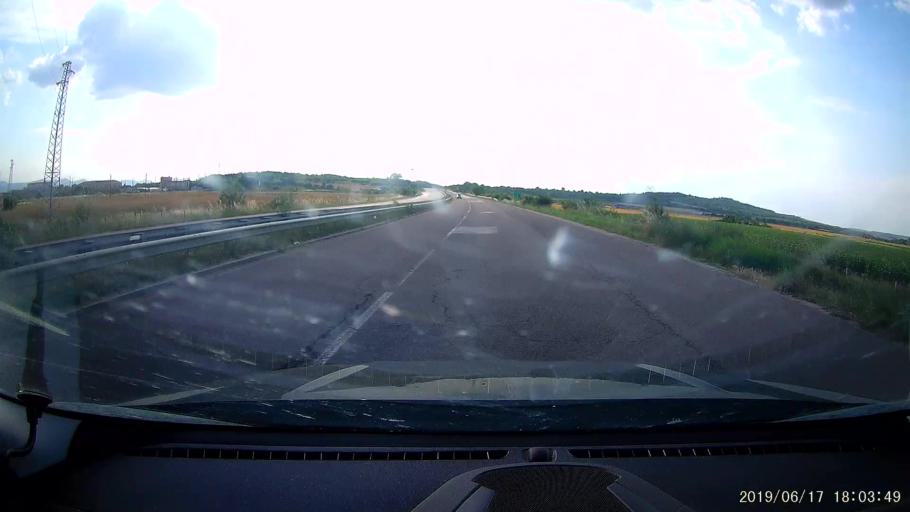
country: BG
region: Khaskovo
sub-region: Obshtina Svilengrad
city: Svilengrad
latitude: 41.7811
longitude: 26.2123
